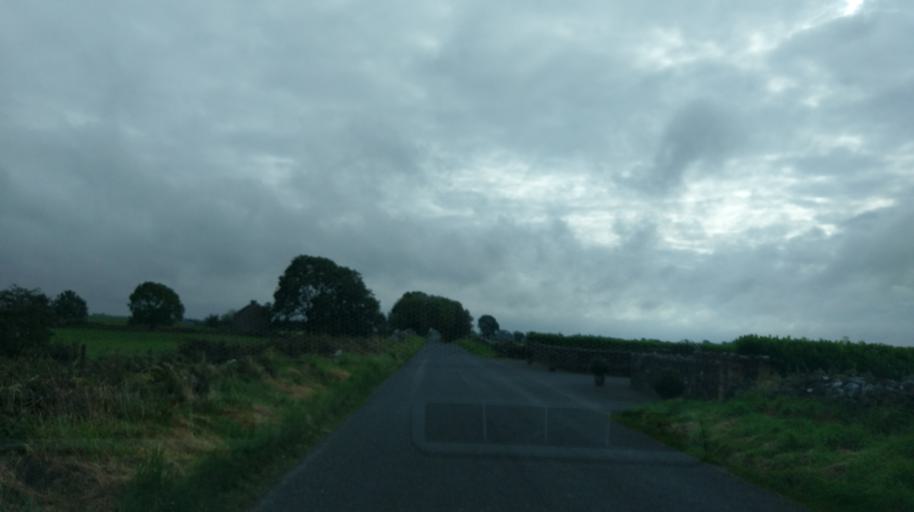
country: IE
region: Connaught
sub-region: County Galway
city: Athenry
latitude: 53.4621
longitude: -8.6267
